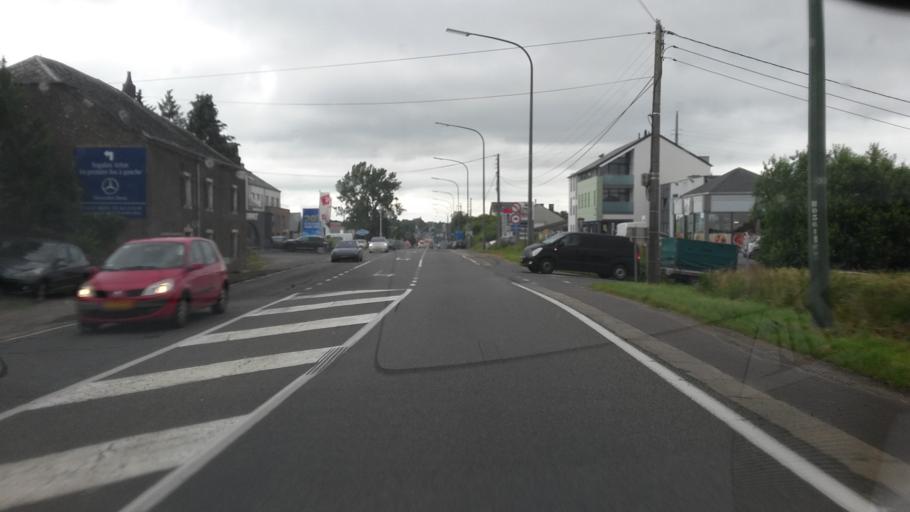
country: BE
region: Wallonia
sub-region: Province du Luxembourg
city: Arlon
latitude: 49.6673
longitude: 5.8241
